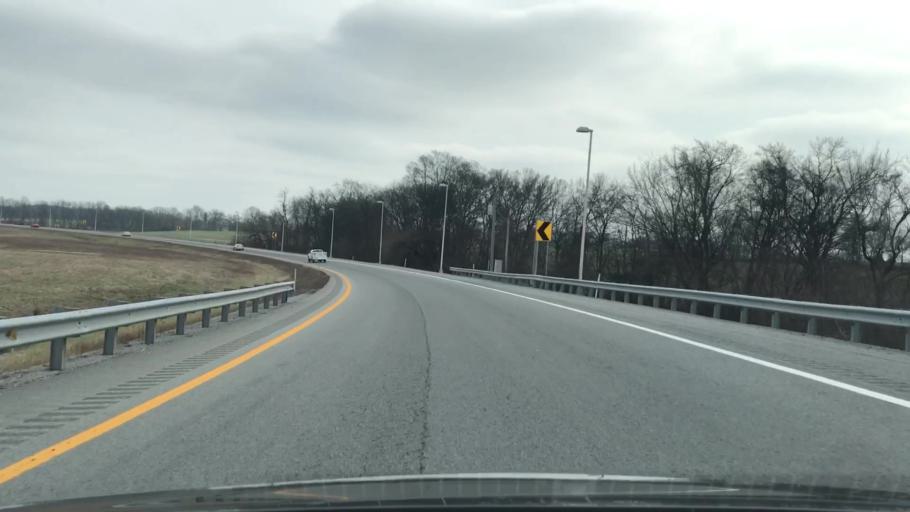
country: US
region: Kentucky
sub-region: Christian County
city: Fort Campbell North
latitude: 36.7413
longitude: -87.5085
